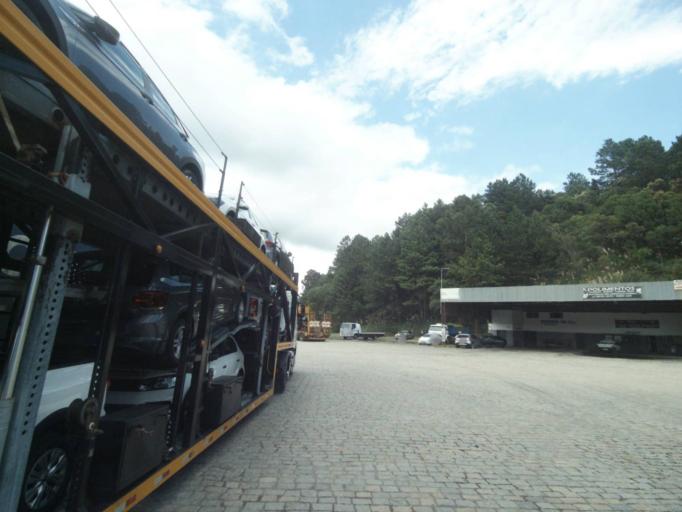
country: BR
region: Parana
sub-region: Campina Grande Do Sul
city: Campina Grande do Sul
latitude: -25.2188
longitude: -48.9048
